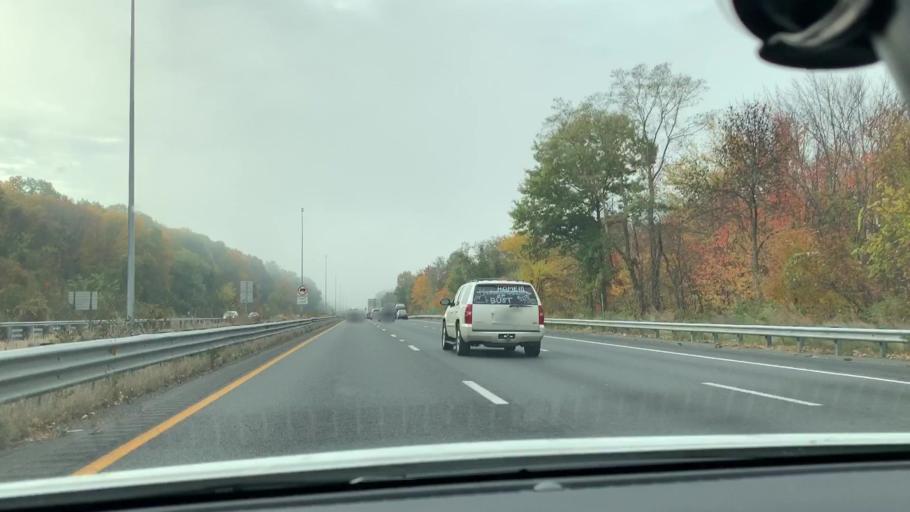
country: US
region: Massachusetts
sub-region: Hampden County
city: Longmeadow
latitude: 42.0521
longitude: -72.5893
